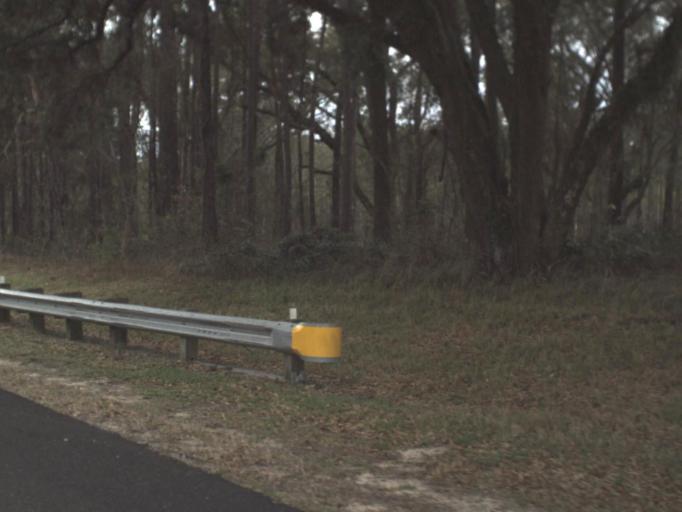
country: US
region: Georgia
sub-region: Grady County
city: Cairo
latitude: 30.6788
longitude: -84.1557
